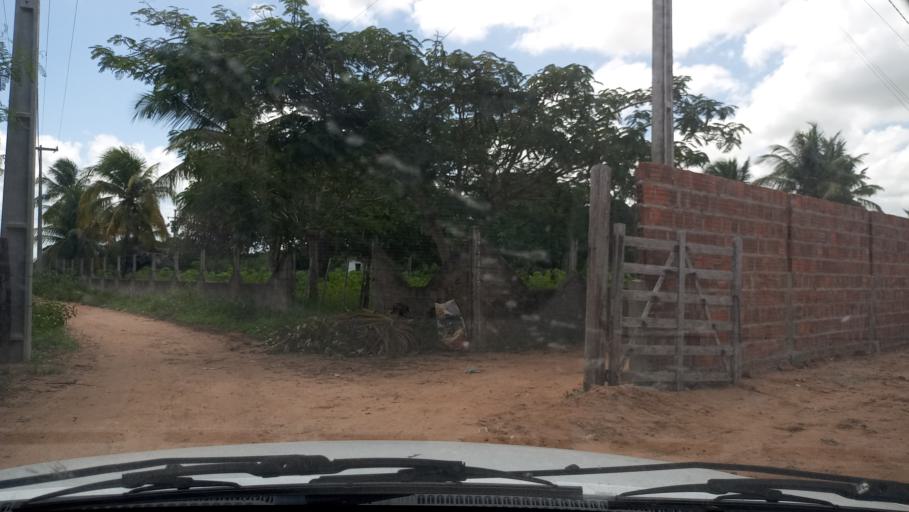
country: BR
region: Rio Grande do Norte
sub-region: Brejinho
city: Brejinho
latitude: -6.2620
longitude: -35.3699
